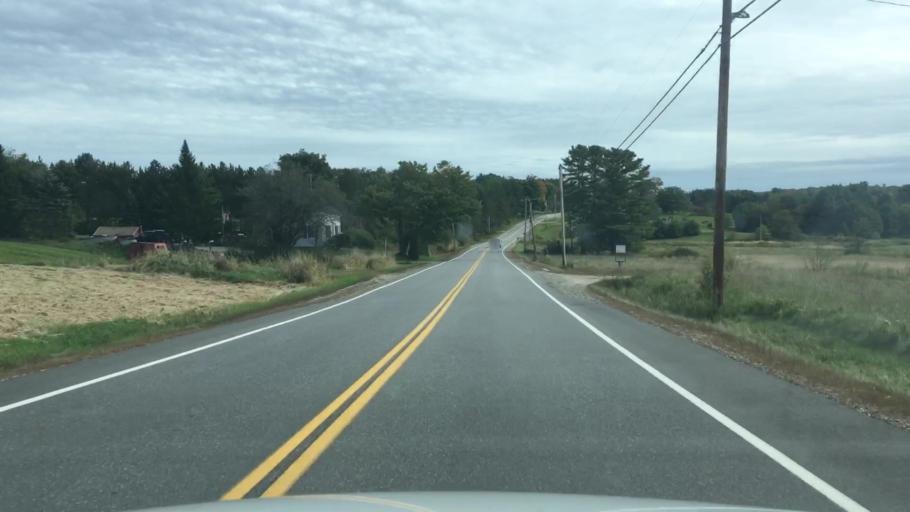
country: US
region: Maine
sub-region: Androscoggin County
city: Lisbon Falls
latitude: 43.9530
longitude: -70.0360
